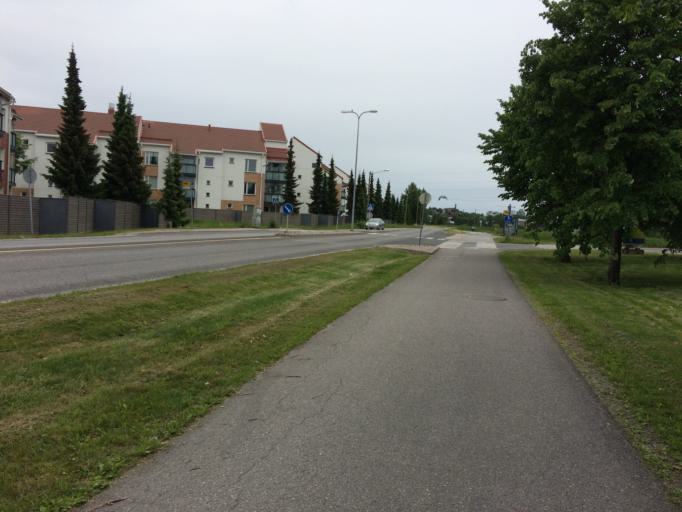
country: FI
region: Varsinais-Suomi
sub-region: Turku
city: Turku
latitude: 60.4696
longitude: 22.3071
